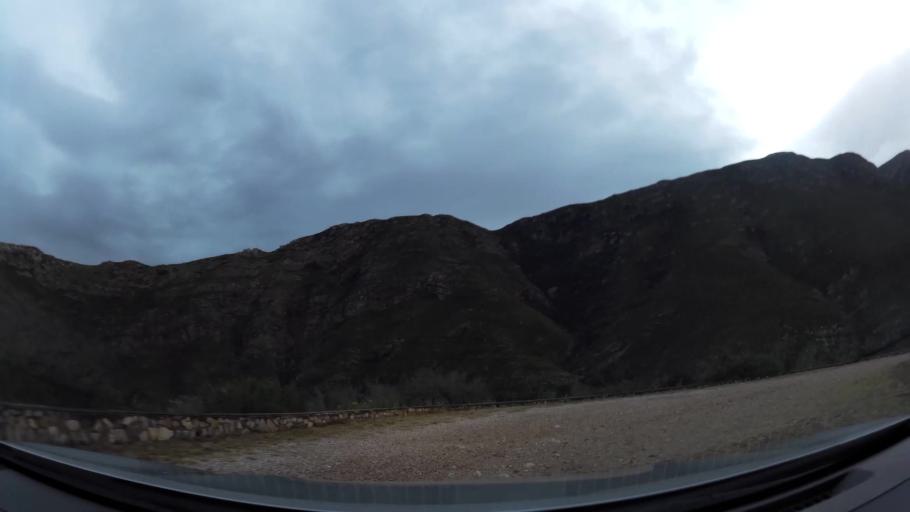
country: ZA
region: Western Cape
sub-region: Overberg District Municipality
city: Swellendam
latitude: -33.9741
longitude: 20.6994
